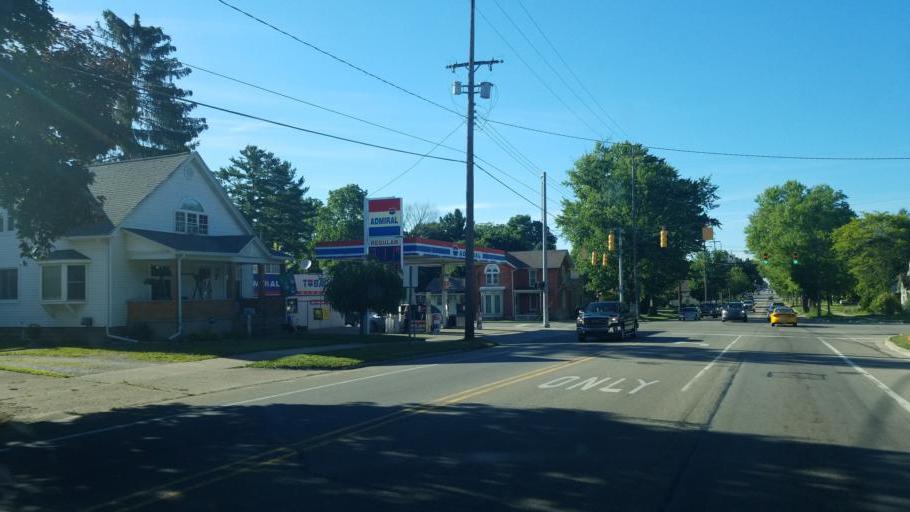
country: US
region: Michigan
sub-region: Eaton County
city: Charlotte
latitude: 42.5530
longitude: -84.8358
